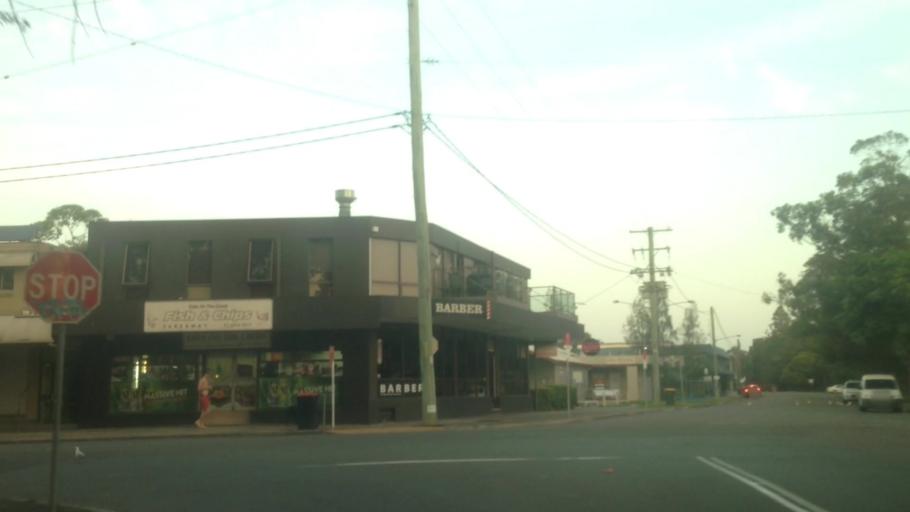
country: AU
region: New South Wales
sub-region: Lake Macquarie Shire
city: Dora Creek
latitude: -33.0843
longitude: 151.5013
